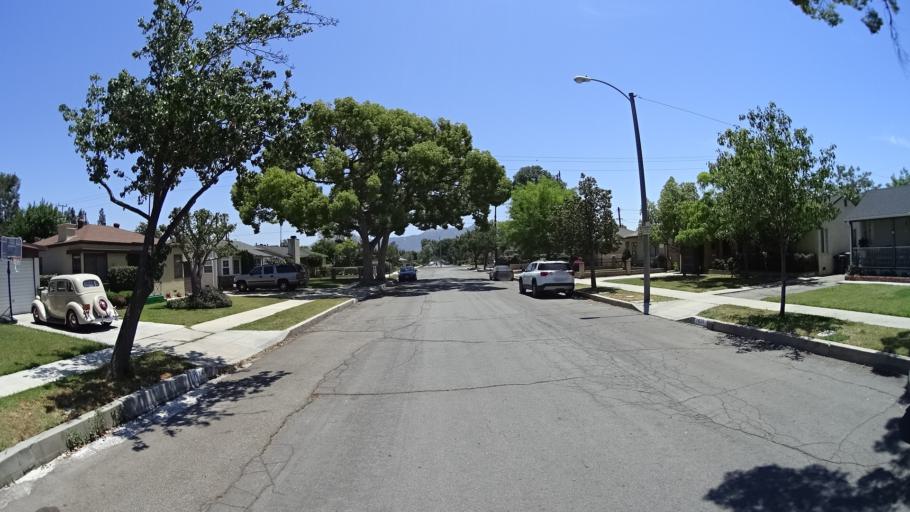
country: US
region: California
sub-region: Los Angeles County
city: Burbank
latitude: 34.1756
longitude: -118.3390
